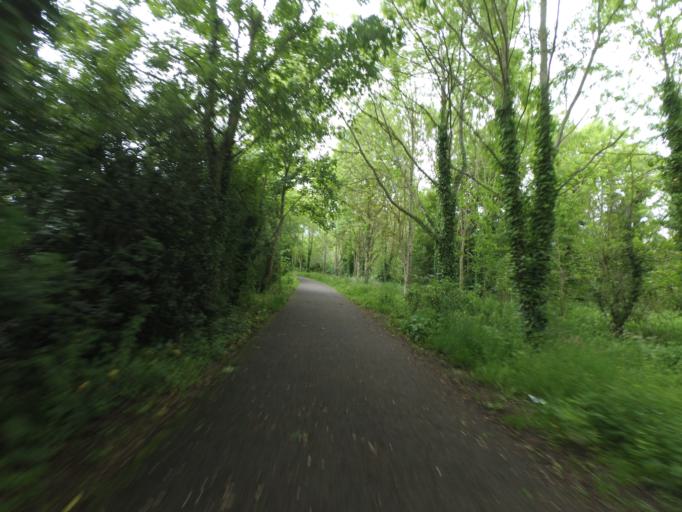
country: GB
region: Scotland
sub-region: East Lothian
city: Musselburgh
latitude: 55.9276
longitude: -3.0498
